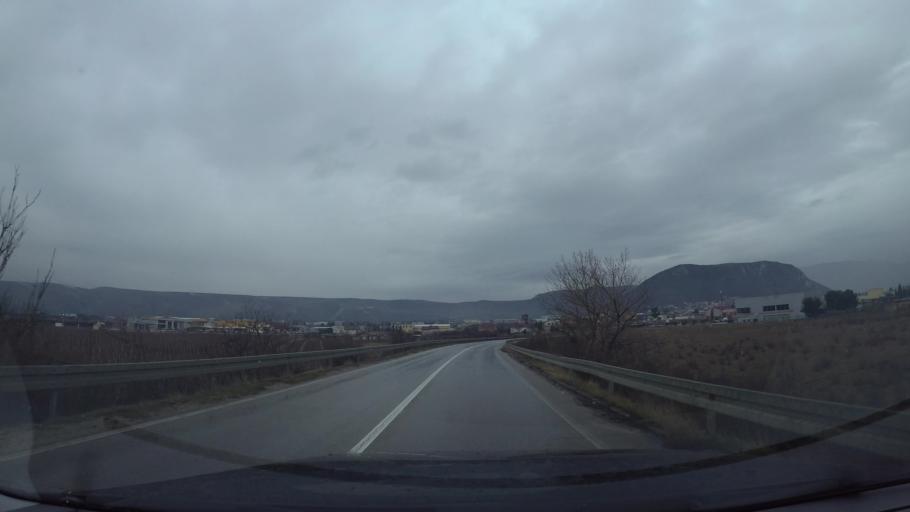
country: BA
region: Federation of Bosnia and Herzegovina
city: Rodoc
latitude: 43.3019
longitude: 17.8357
